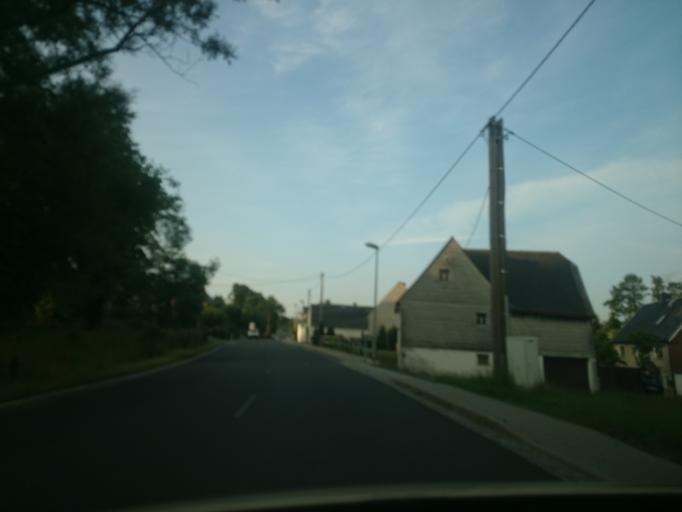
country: DE
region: Saxony
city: Grosshartmannsdorf
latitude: 50.7900
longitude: 13.3181
